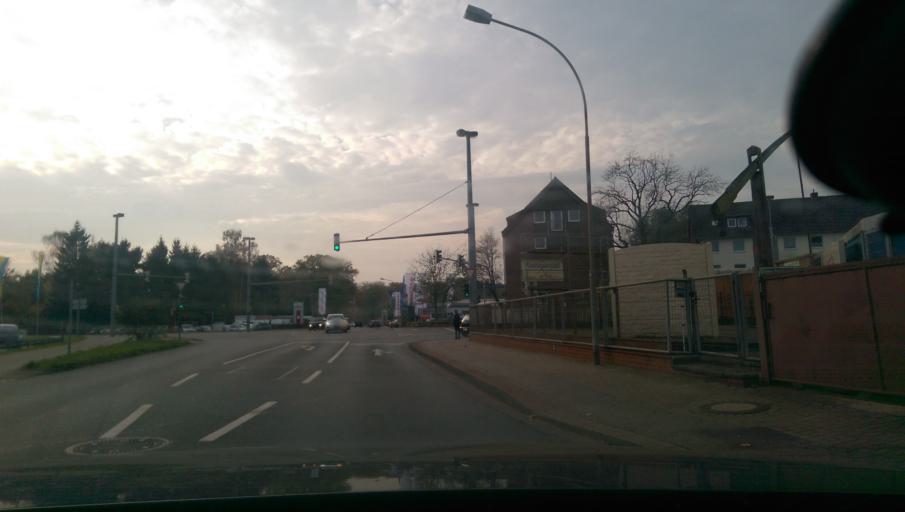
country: DE
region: Lower Saxony
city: Celle
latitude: 52.6022
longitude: 10.0721
